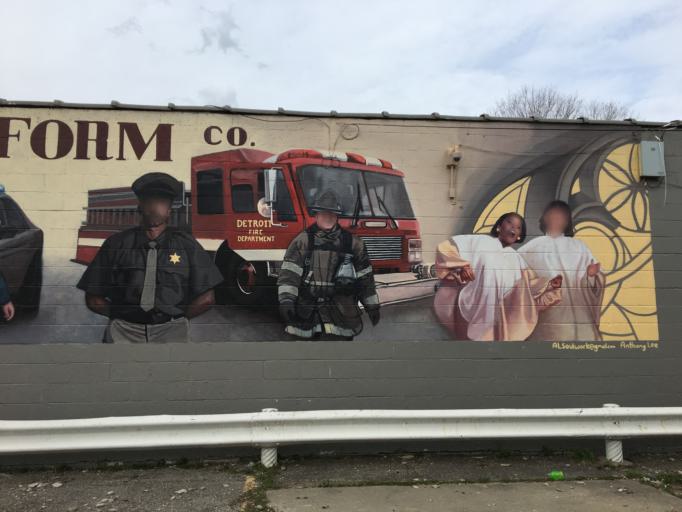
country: US
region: Michigan
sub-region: Wayne County
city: Hamtramck
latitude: 42.3737
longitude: -83.0651
